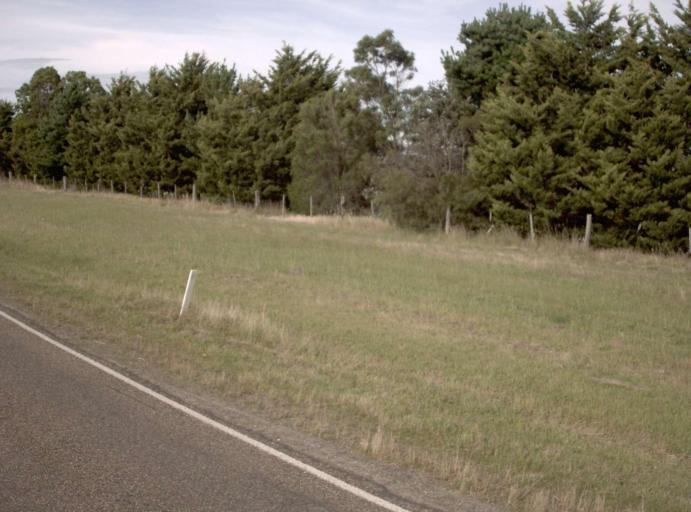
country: AU
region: Victoria
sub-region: Wellington
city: Heyfield
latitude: -38.0397
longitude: 146.6660
